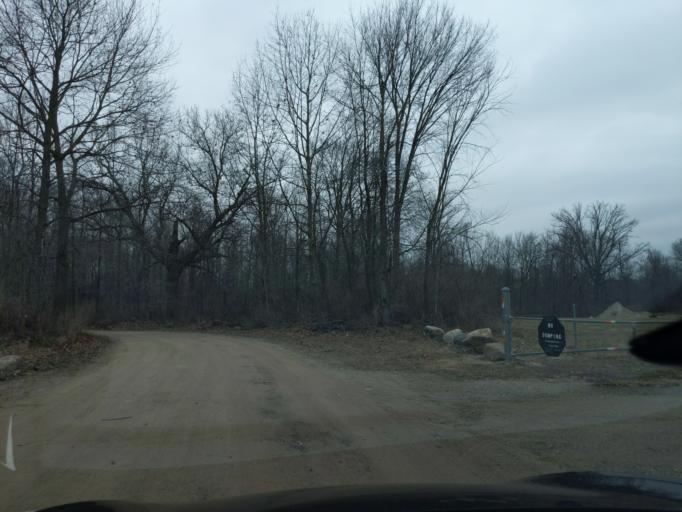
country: US
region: Michigan
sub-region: Eaton County
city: Potterville
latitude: 42.6193
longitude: -84.7570
